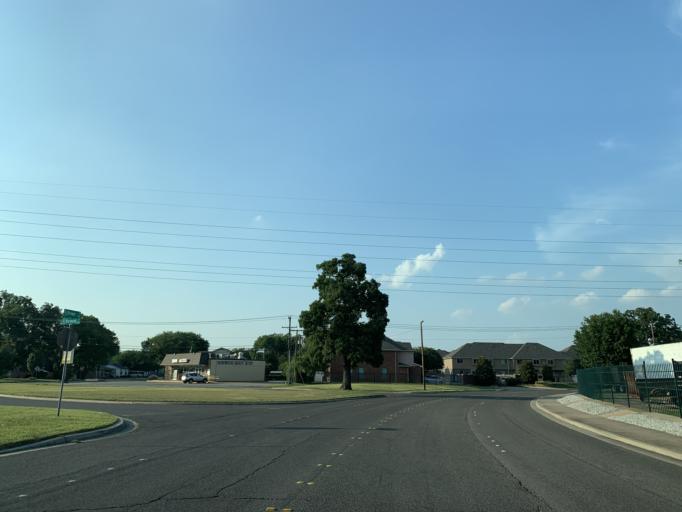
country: US
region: Texas
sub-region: Tarrant County
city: Hurst
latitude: 32.8106
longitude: -97.1691
